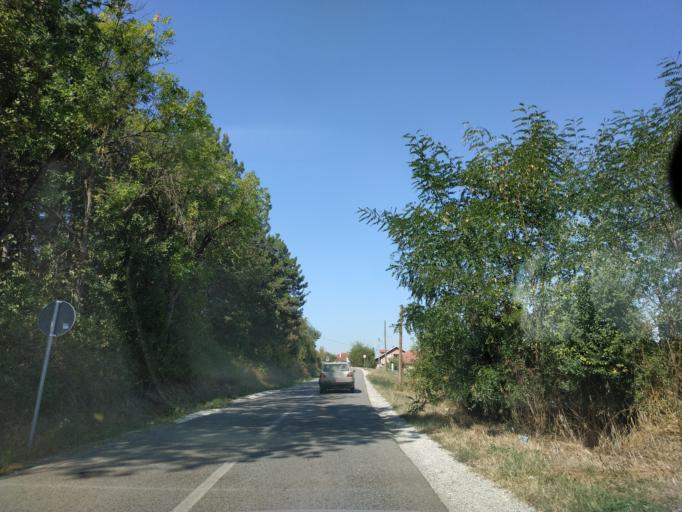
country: RS
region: Central Serbia
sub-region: Sumadijski Okrug
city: Topola
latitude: 44.2782
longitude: 20.6215
